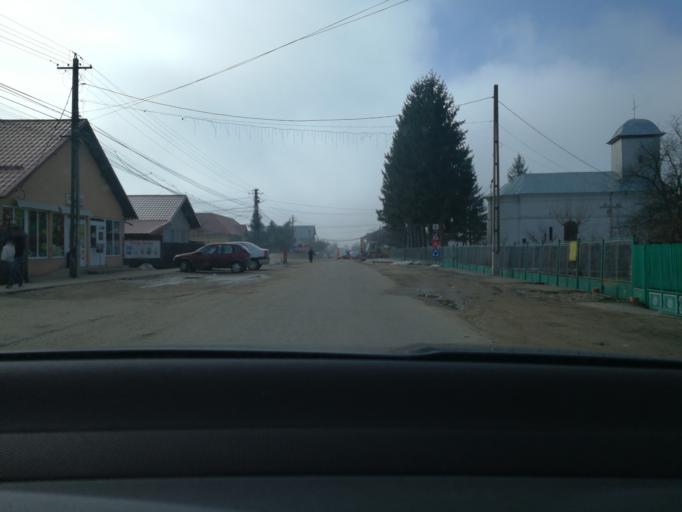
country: RO
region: Prahova
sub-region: Comuna Magureni
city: Lunca Prahovei
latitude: 45.0445
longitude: 25.7511
